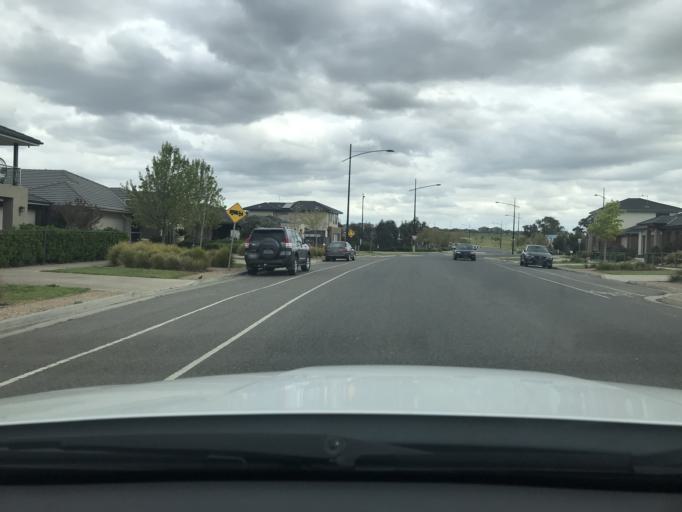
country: AU
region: Victoria
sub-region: Hume
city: Roxburgh Park
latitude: -37.5937
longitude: 144.8943
